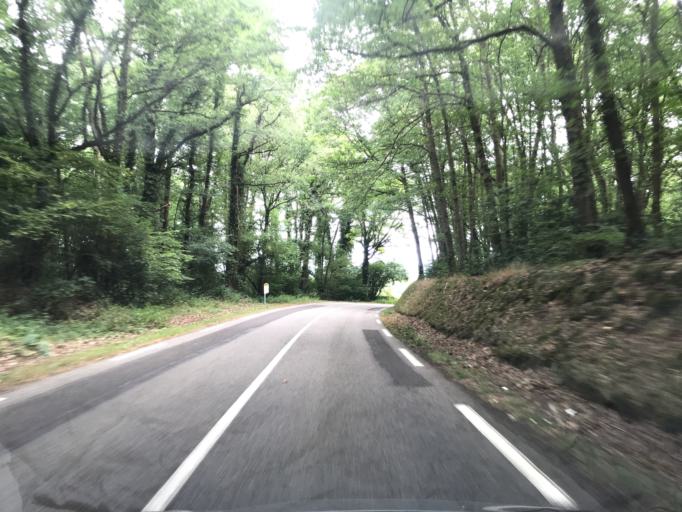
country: FR
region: Haute-Normandie
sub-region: Departement de l'Eure
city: Menilles
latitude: 49.0419
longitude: 1.3051
